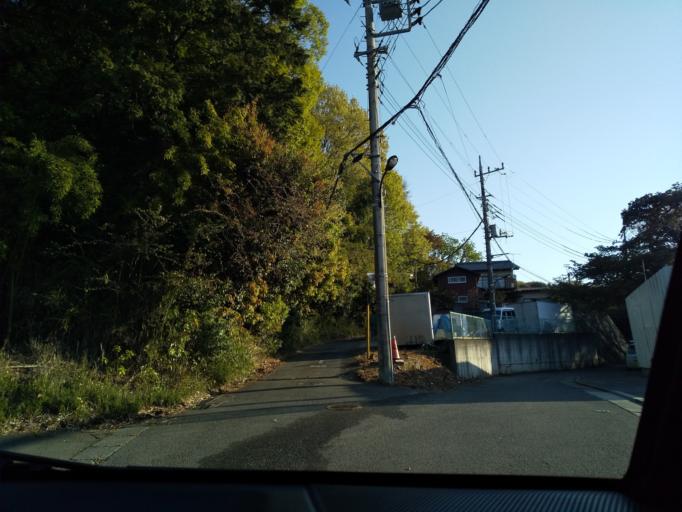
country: JP
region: Tokyo
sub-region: Machida-shi
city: Machida
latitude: 35.6048
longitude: 139.4340
